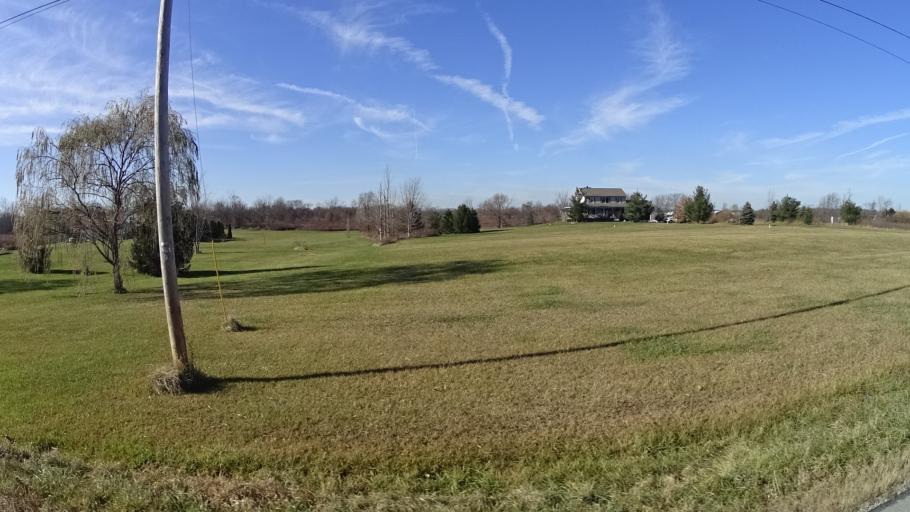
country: US
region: Ohio
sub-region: Huron County
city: New London
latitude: 41.0700
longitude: -82.3042
